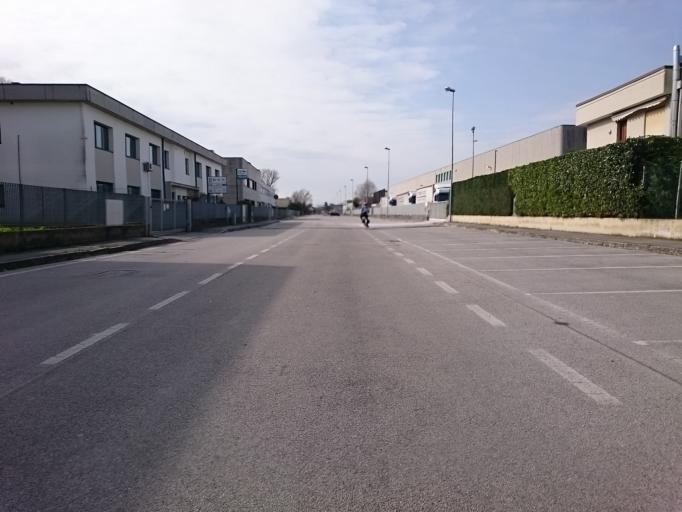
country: IT
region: Veneto
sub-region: Provincia di Padova
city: Terradura
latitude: 45.3453
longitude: 11.8344
